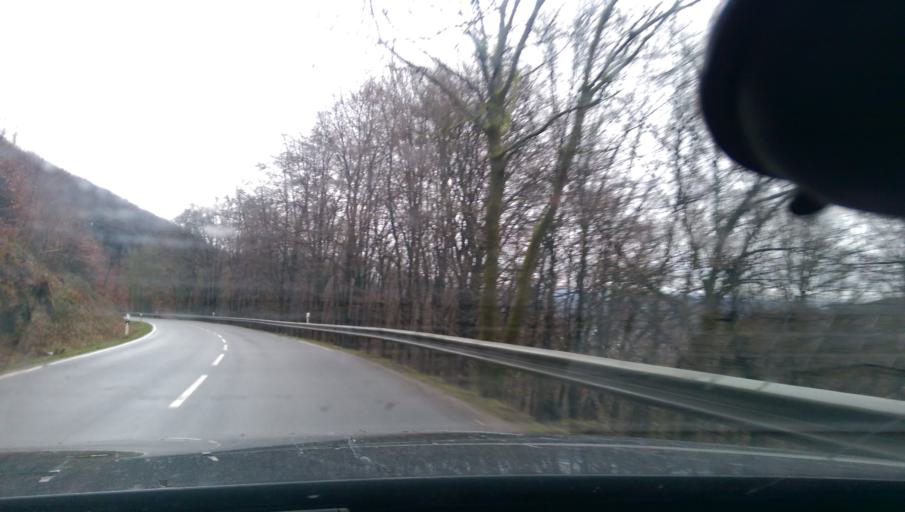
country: DE
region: North Rhine-Westphalia
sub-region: Regierungsbezirk Arnsberg
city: Finnentrop
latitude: 51.2372
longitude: 7.9474
